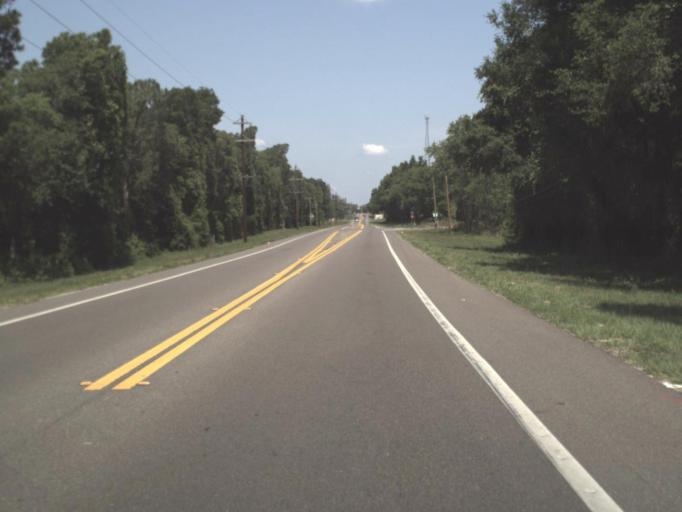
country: US
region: Florida
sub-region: Clay County
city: Keystone Heights
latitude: 29.7981
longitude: -82.0515
